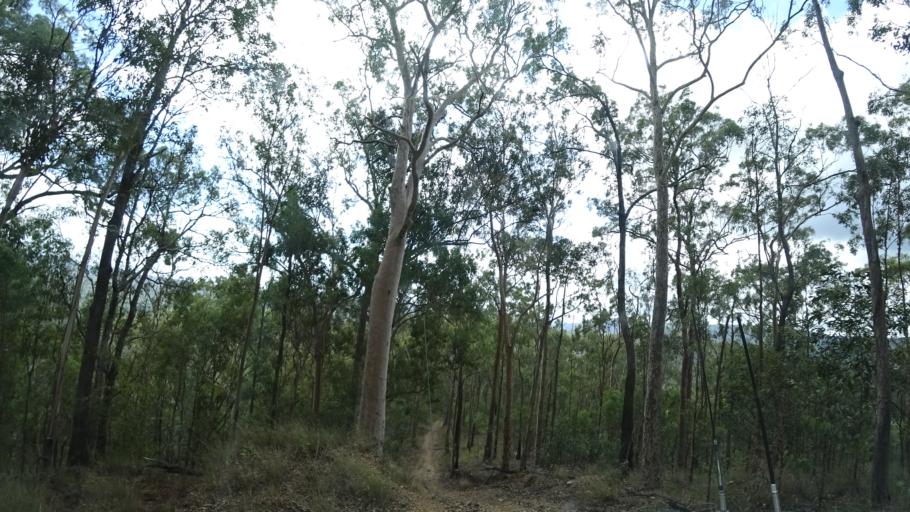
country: AU
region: Queensland
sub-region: Moreton Bay
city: Highvale
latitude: -27.3777
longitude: 152.7377
